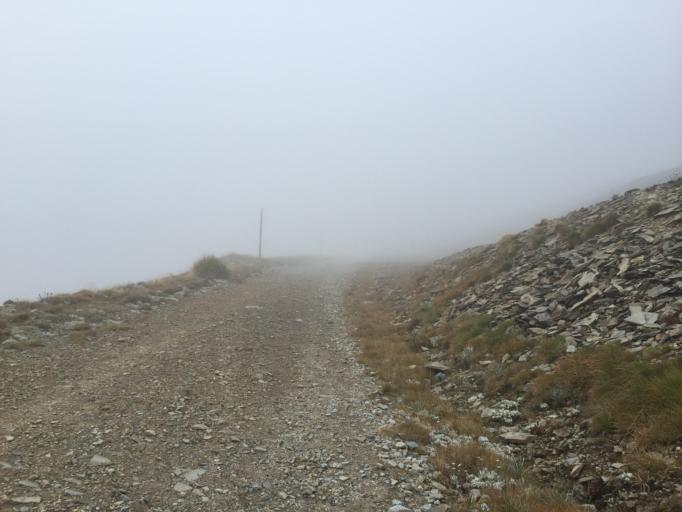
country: AU
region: New South Wales
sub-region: Snowy River
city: Jindabyne
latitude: -36.4538
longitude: 148.2736
